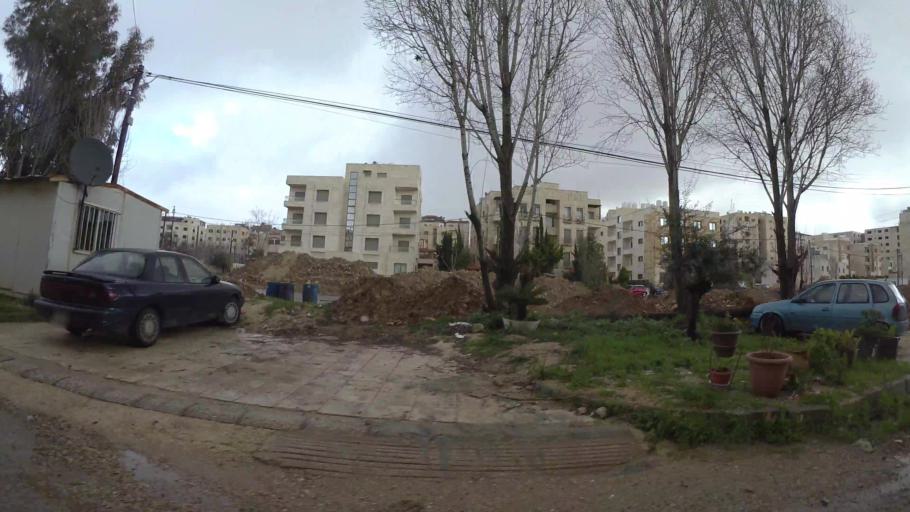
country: JO
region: Amman
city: Wadi as Sir
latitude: 31.9424
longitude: 35.8520
